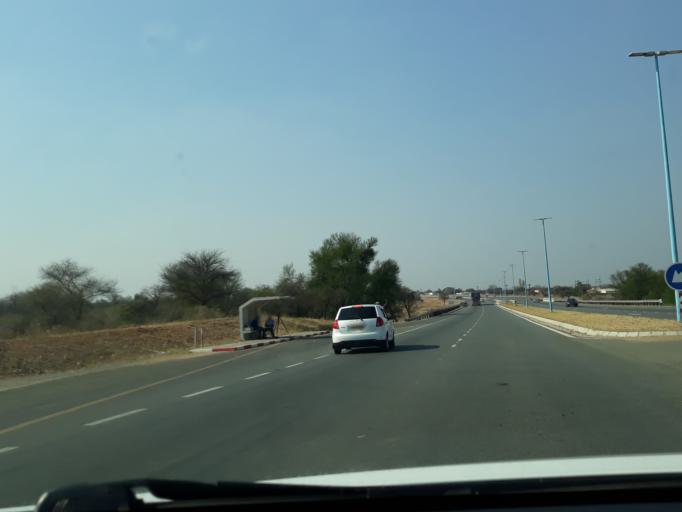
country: BW
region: Central
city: Tonota
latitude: -21.4105
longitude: 27.4507
